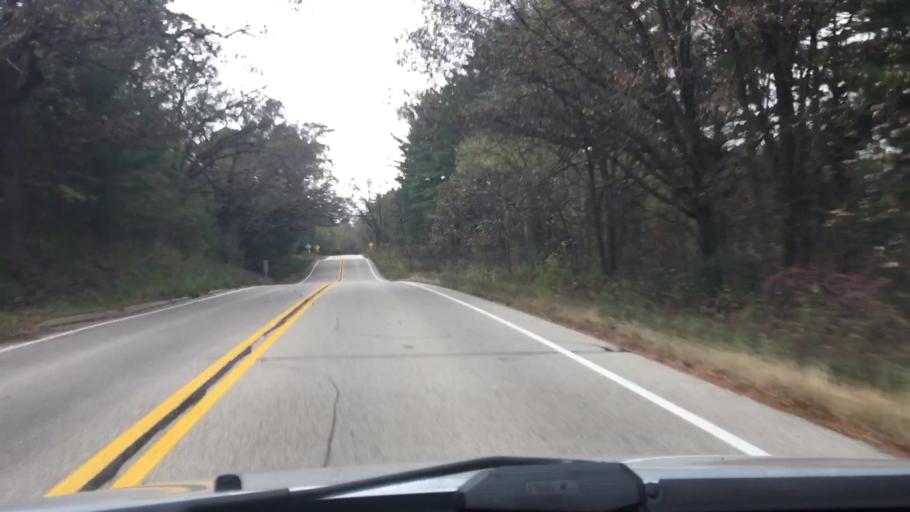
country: US
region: Wisconsin
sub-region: Waukesha County
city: Eagle
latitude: 42.9220
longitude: -88.4700
